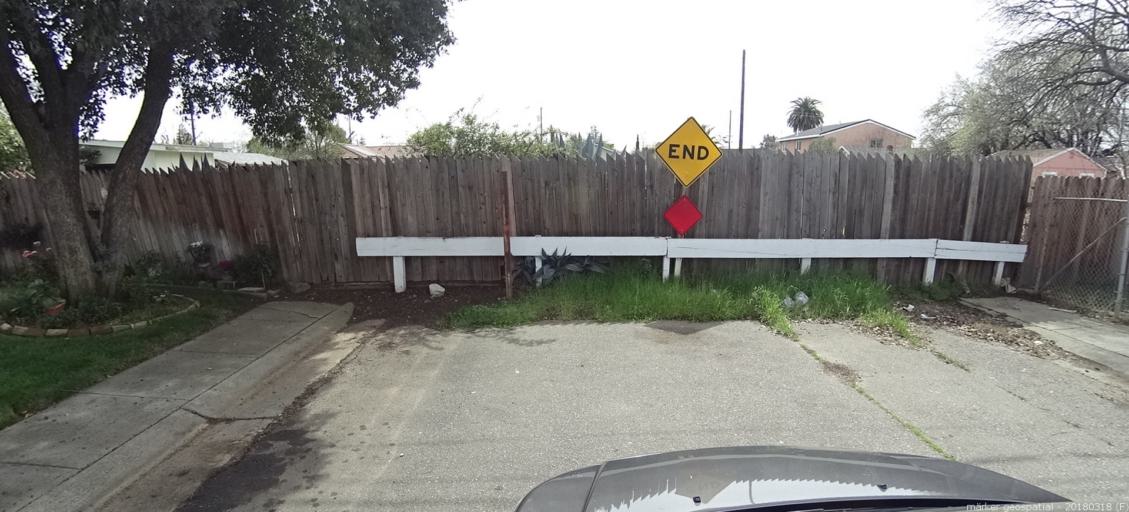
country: US
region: California
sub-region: Sacramento County
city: Parkway
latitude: 38.5360
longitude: -121.4517
